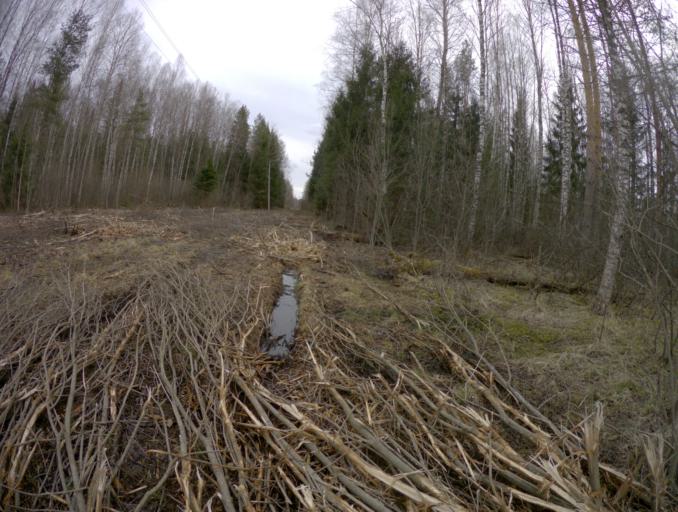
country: RU
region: Vladimir
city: Raduzhnyy
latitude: 55.8760
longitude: 40.2106
